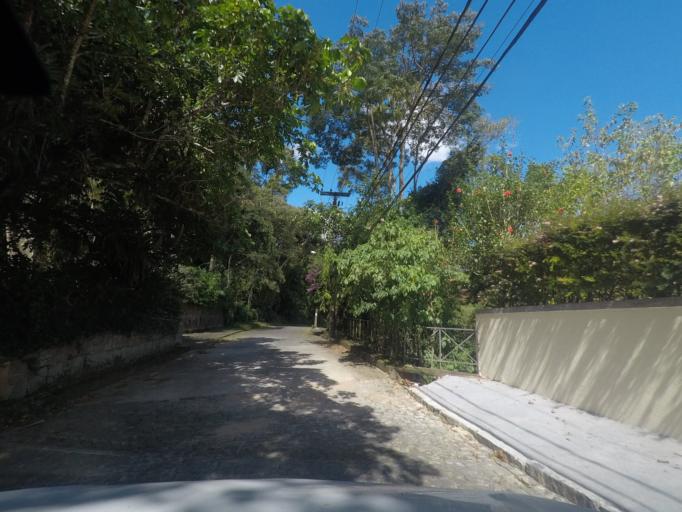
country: BR
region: Rio de Janeiro
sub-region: Teresopolis
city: Teresopolis
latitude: -22.4334
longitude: -42.9882
